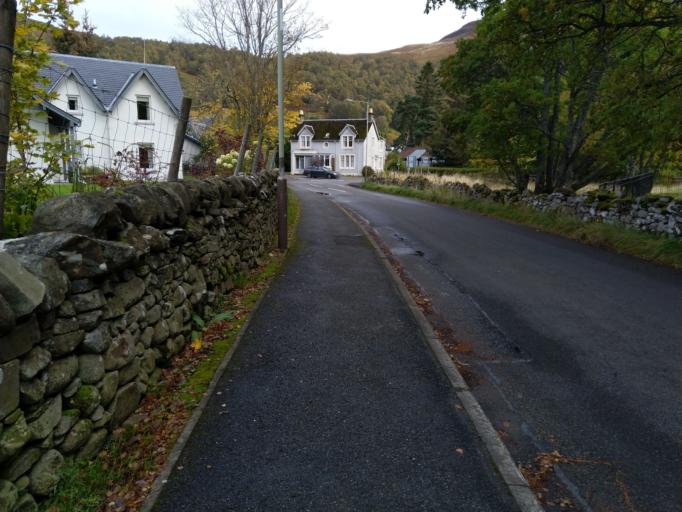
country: GB
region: Scotland
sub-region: Perth and Kinross
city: Aberfeldy
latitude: 56.6986
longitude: -4.1855
